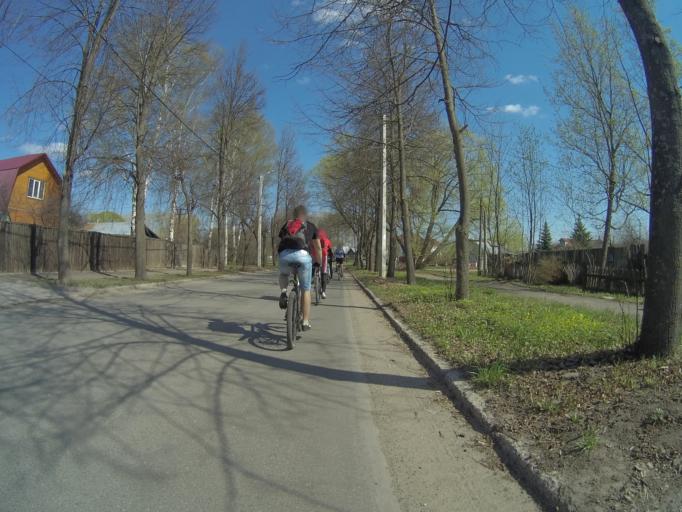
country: RU
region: Vladimir
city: Suzdal'
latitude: 56.4225
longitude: 40.4553
